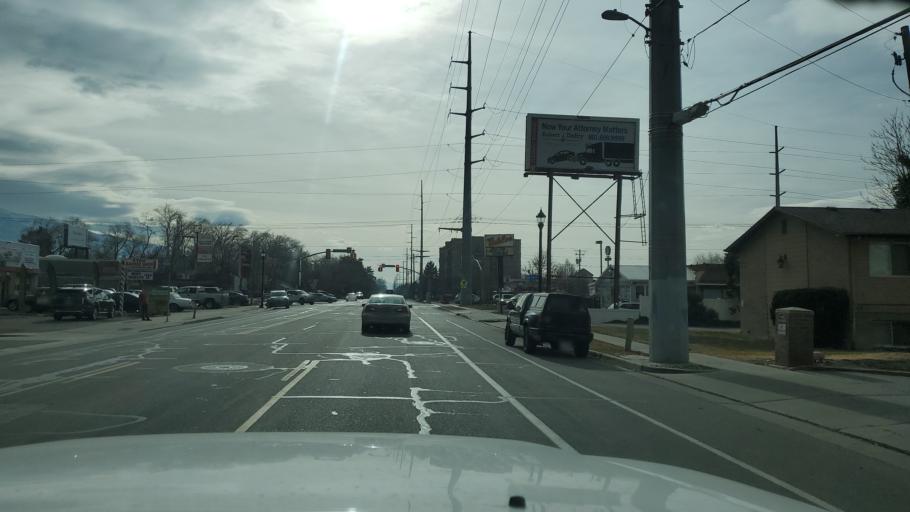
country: US
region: Utah
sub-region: Salt Lake County
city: Millcreek
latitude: 40.6880
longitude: -111.8656
